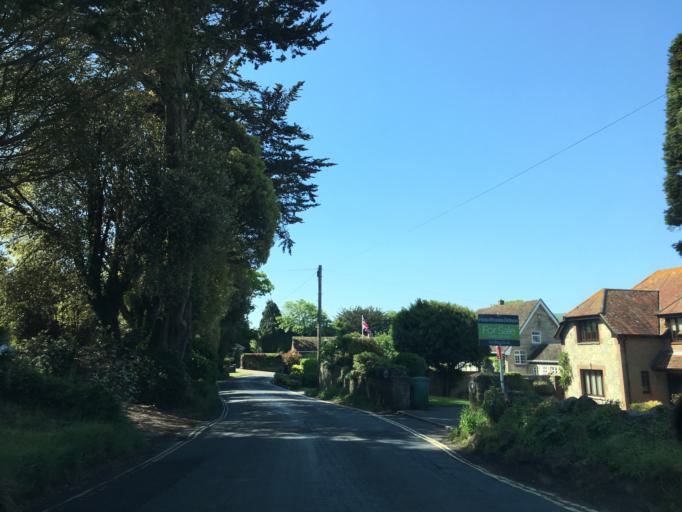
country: GB
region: England
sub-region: Isle of Wight
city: Newchurch
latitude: 50.6324
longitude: -1.2209
